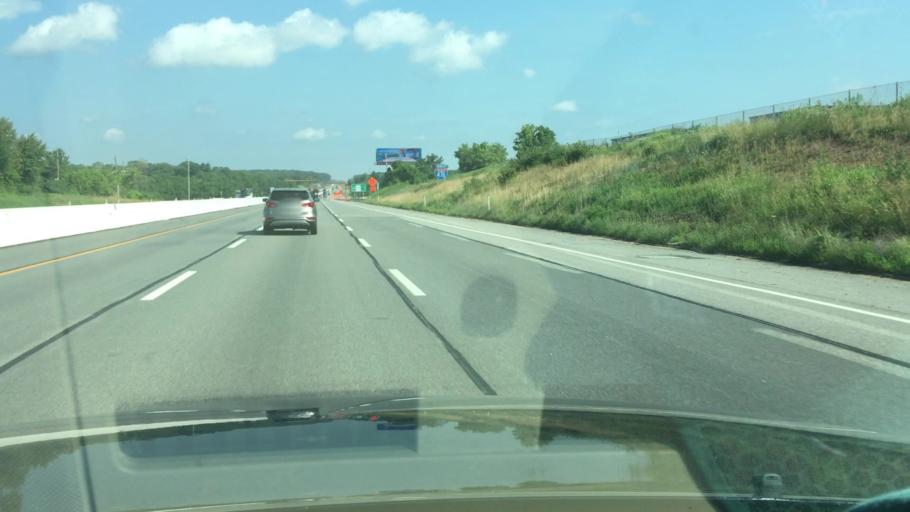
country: US
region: Pennsylvania
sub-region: Montgomery County
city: Kulpsville
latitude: 40.2570
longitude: -75.3501
